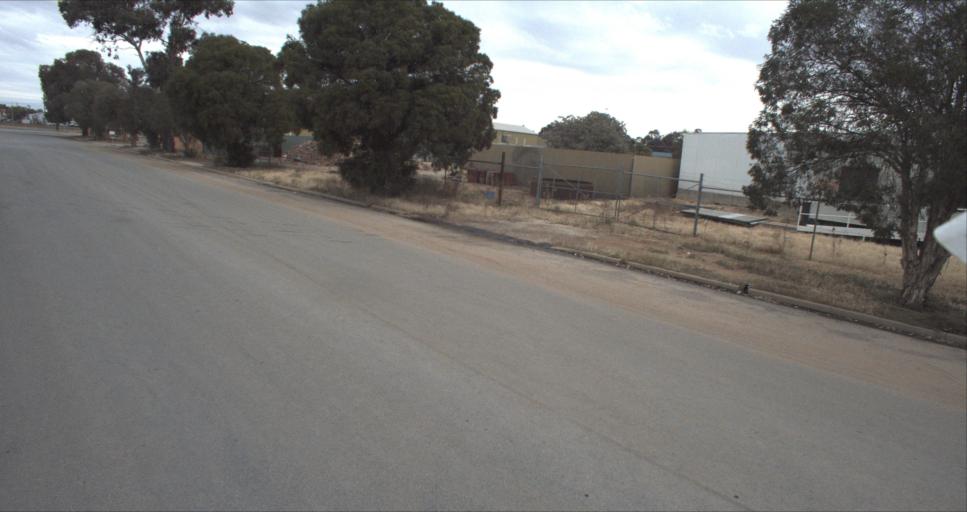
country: AU
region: New South Wales
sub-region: Leeton
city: Leeton
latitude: -34.5497
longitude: 146.3905
